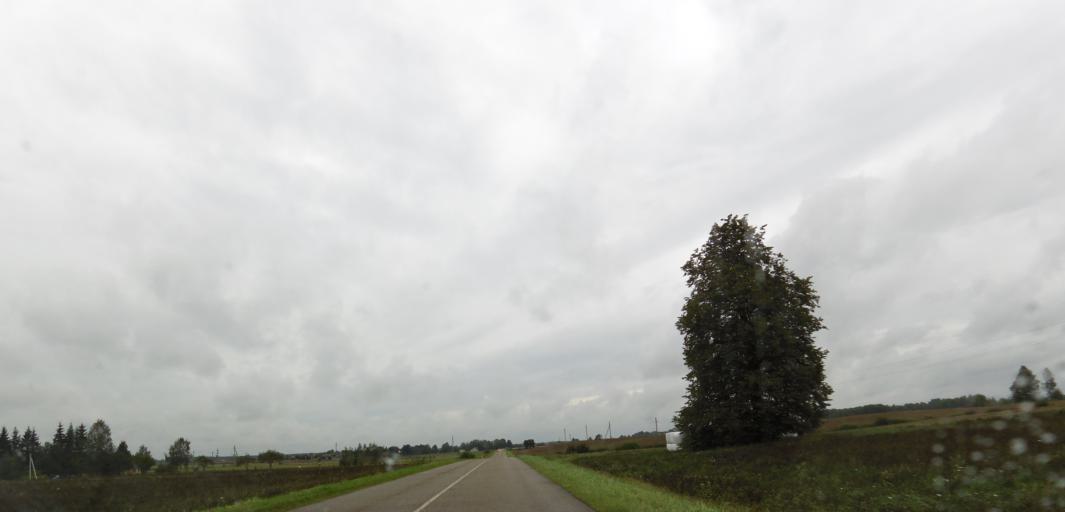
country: LT
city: Sirvintos
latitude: 55.0801
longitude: 25.0083
